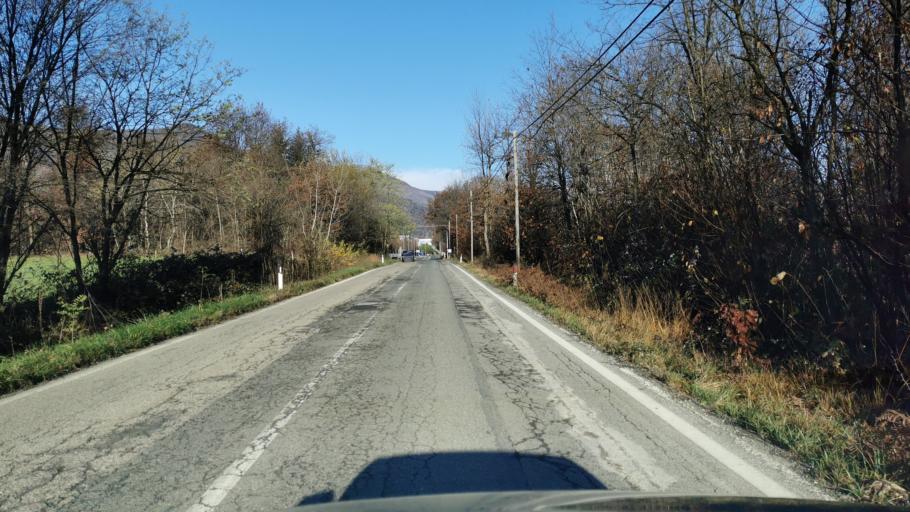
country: IT
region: Piedmont
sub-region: Provincia di Torino
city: La Cassa
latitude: 45.1663
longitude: 7.5255
